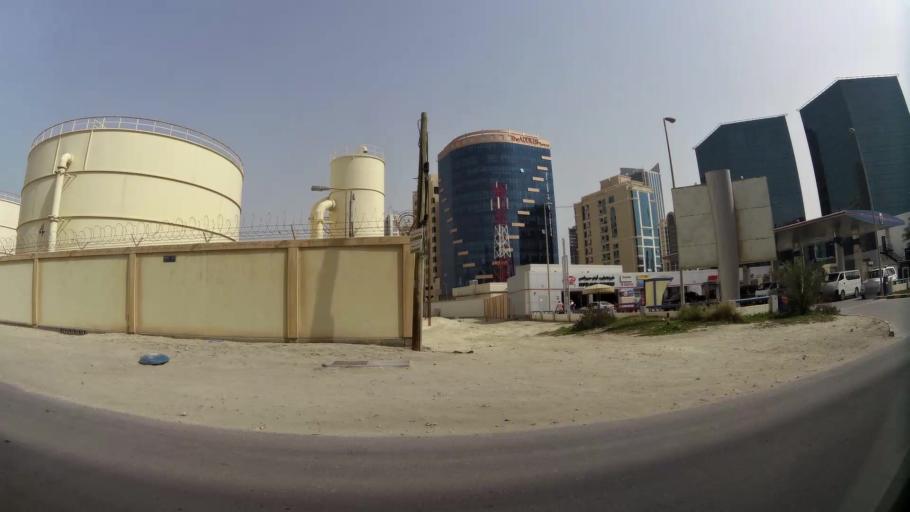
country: BH
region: Manama
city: Jidd Hafs
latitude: 26.2381
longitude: 50.5333
